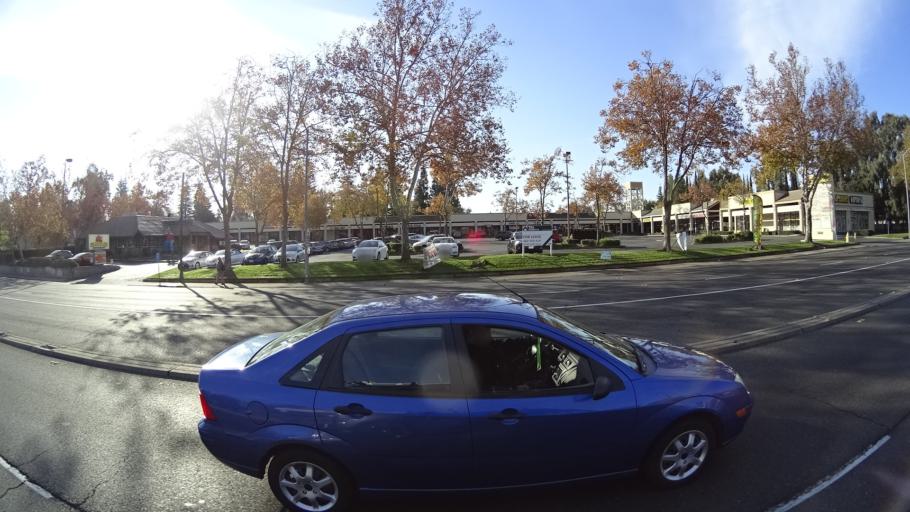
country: US
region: California
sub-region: Sacramento County
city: Foothill Farms
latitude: 38.6607
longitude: -121.3287
